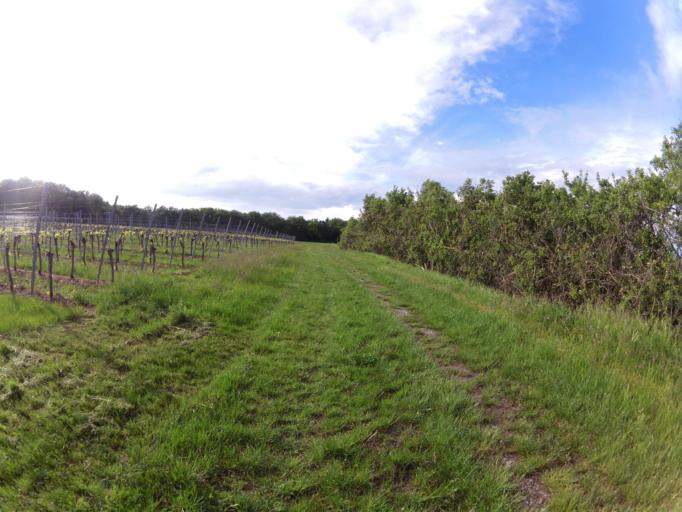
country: DE
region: Bavaria
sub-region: Regierungsbezirk Unterfranken
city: Volkach
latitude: 49.8800
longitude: 10.2664
